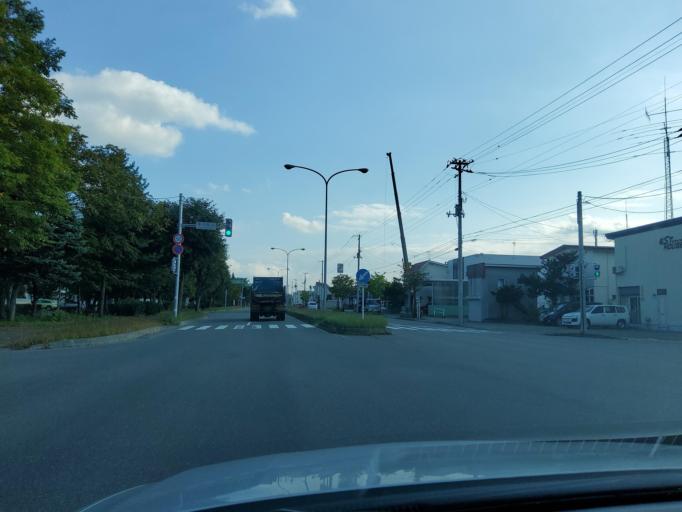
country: JP
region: Hokkaido
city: Obihiro
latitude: 42.9104
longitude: 143.2134
